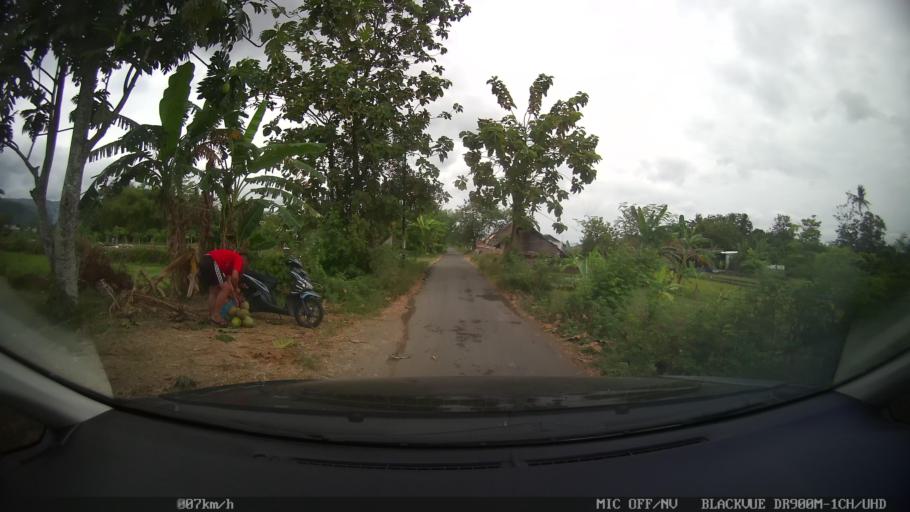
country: ID
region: Daerah Istimewa Yogyakarta
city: Sewon
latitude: -7.8535
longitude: 110.4164
